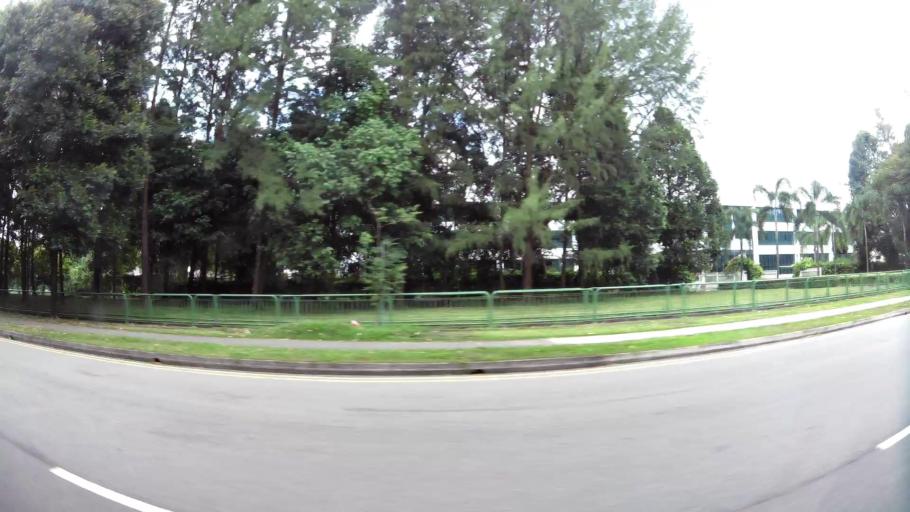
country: MY
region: Johor
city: Kampung Pasir Gudang Baru
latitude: 1.4594
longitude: 103.8222
